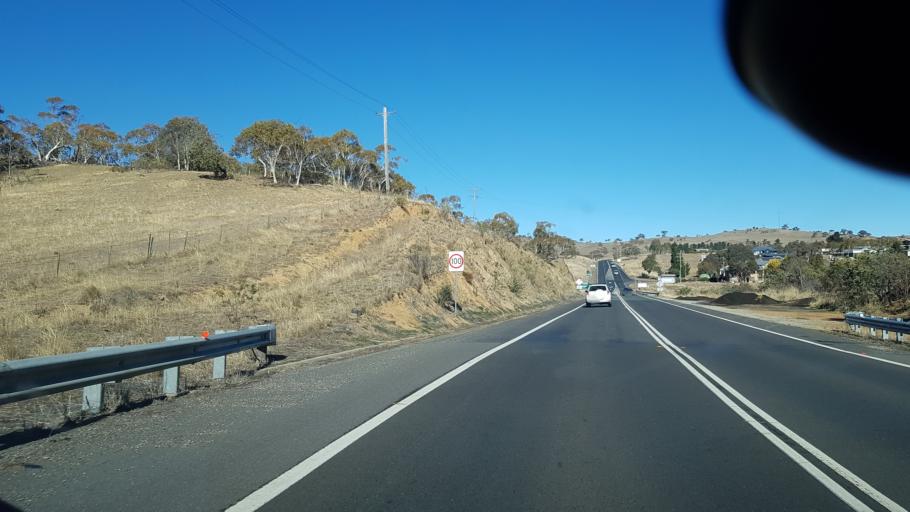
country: AU
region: New South Wales
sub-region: Snowy River
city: Jindabyne
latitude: -36.3994
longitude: 148.6537
